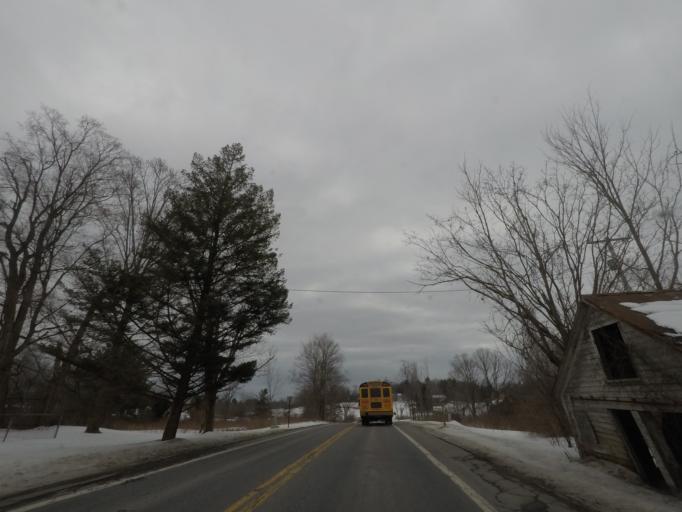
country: US
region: New York
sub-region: Saratoga County
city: Stillwater
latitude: 42.9624
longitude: -73.6747
